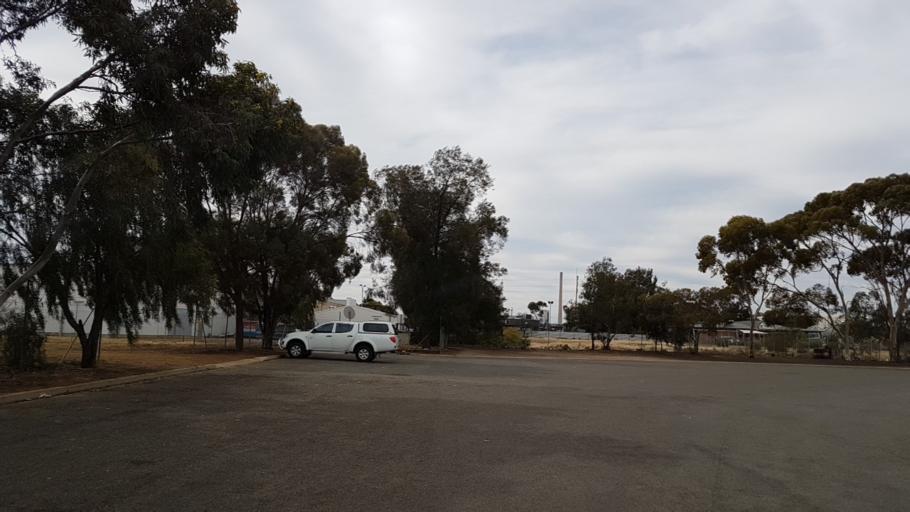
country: AU
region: South Australia
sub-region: Port Pirie City and Dists
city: Port Pirie
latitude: -33.1919
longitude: 138.0081
